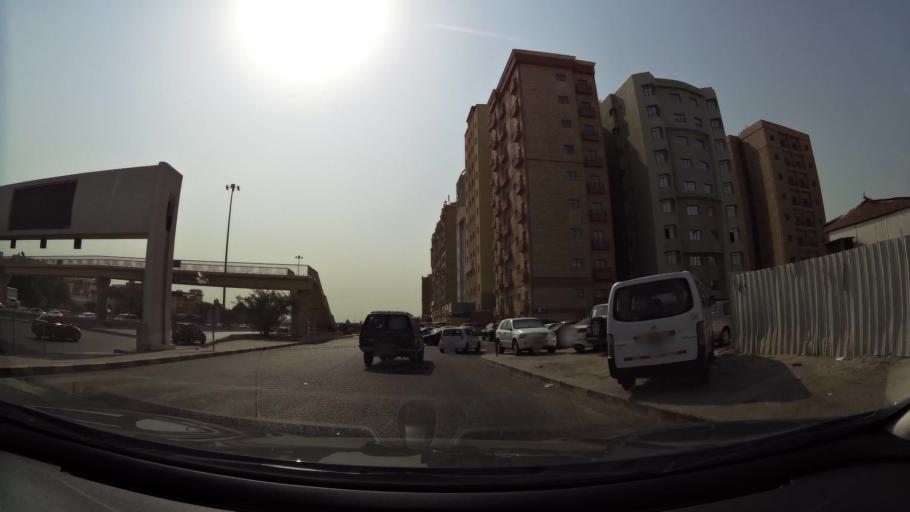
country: KW
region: Muhafazat Hawalli
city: Ar Rumaythiyah
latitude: 29.3197
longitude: 48.0594
